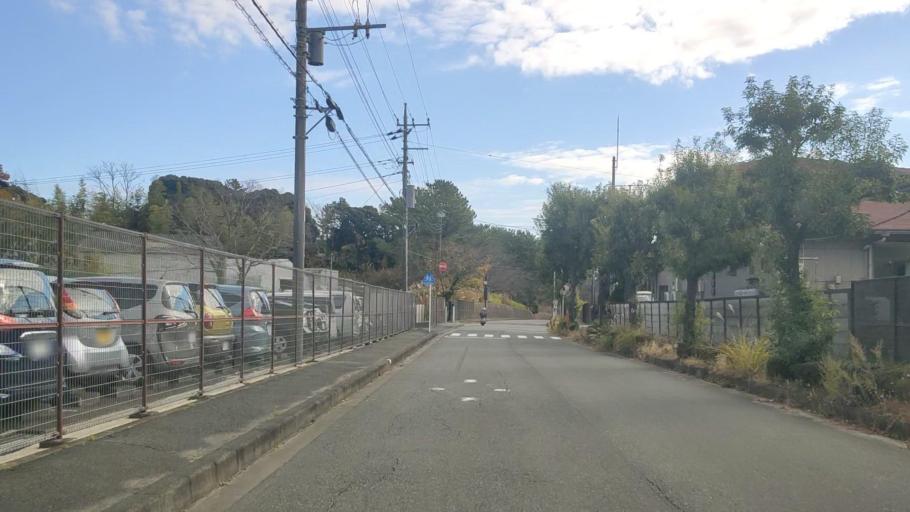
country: JP
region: Kanagawa
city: Yokohama
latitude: 35.4479
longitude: 139.5470
